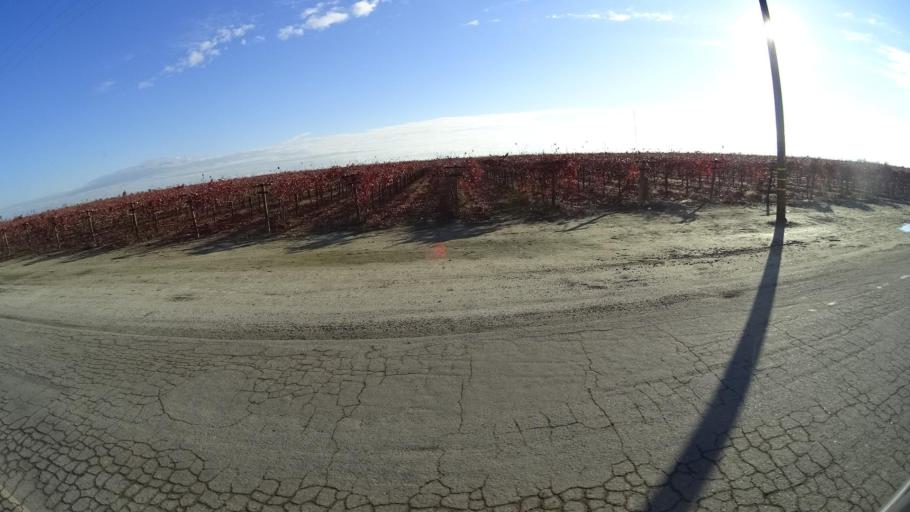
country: US
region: California
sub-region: Kern County
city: Delano
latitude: 35.7625
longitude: -119.2852
